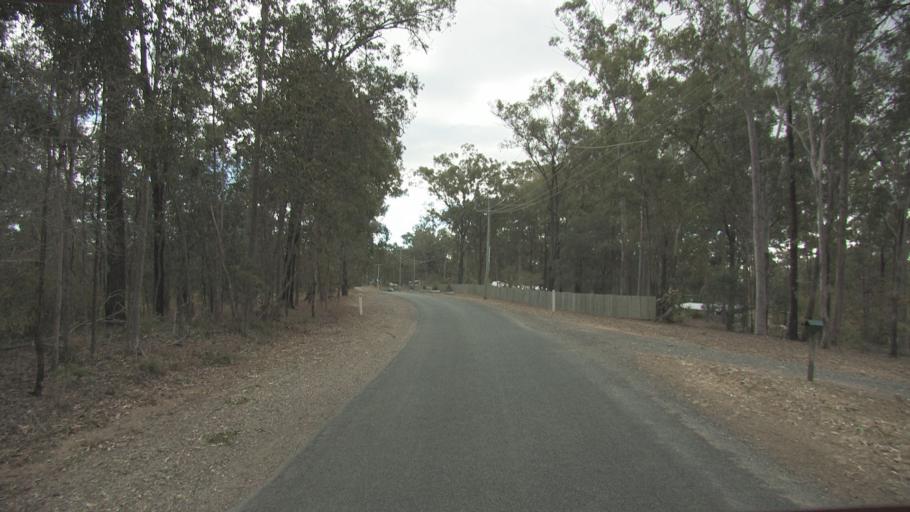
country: AU
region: Queensland
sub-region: Logan
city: Cedar Vale
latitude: -27.8830
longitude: 153.0373
